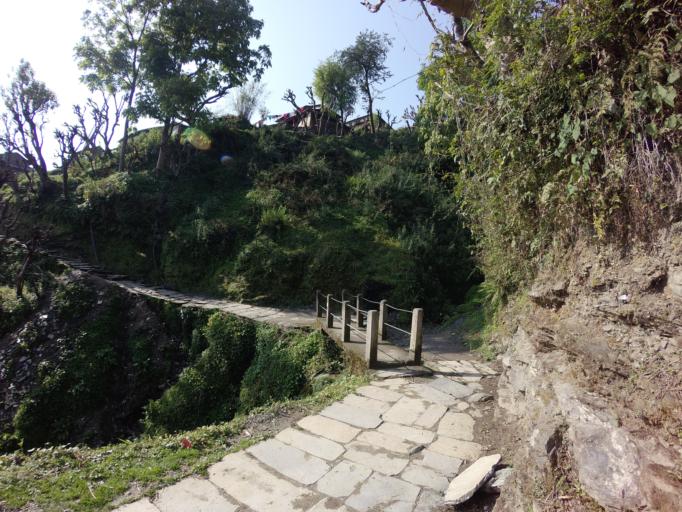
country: NP
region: Western Region
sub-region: Dhawalagiri Zone
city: Chitre
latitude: 28.3780
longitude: 83.8075
